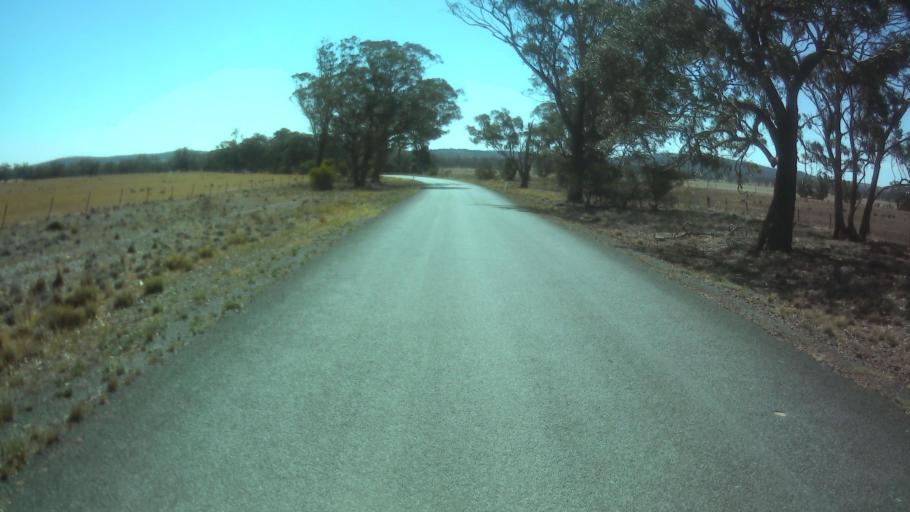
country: AU
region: New South Wales
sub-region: Weddin
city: Grenfell
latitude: -33.8095
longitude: 147.9122
